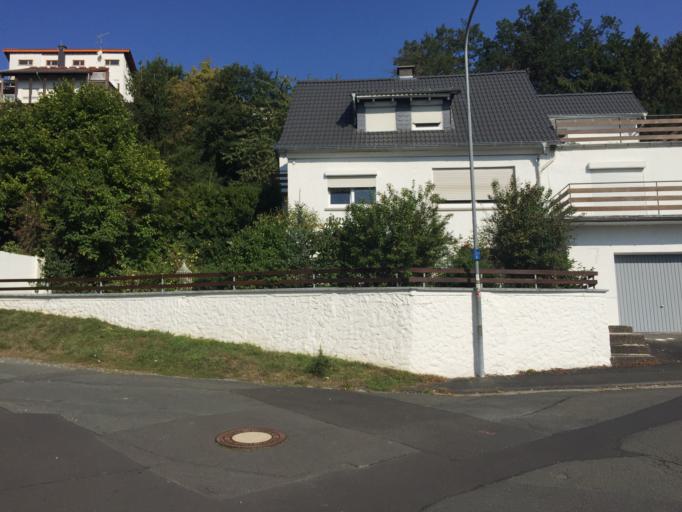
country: DE
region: Hesse
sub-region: Regierungsbezirk Giessen
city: Schoeffengrund
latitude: 50.4513
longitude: 8.5562
